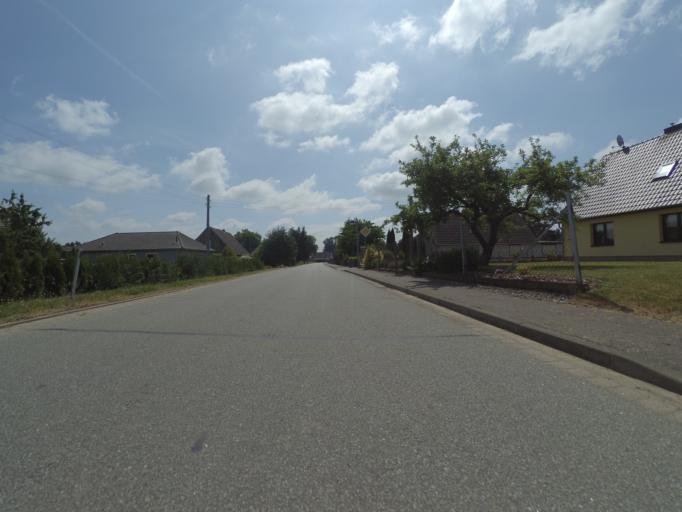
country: DE
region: Mecklenburg-Vorpommern
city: Siggelkow
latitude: 53.4246
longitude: 11.9703
